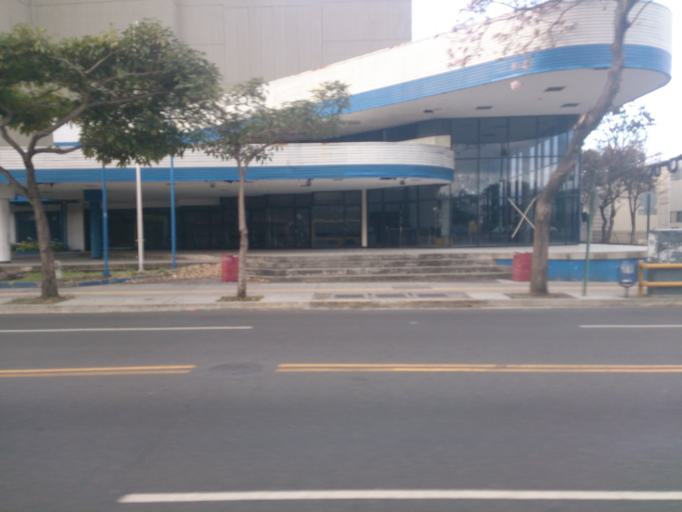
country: CR
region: San Jose
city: San Jose
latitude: 9.9353
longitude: -84.0891
